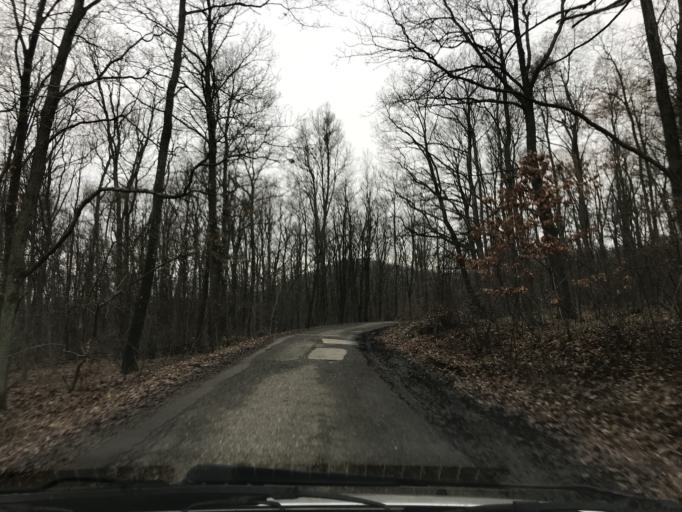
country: HU
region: Pest
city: Nagykovacsi
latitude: 47.6884
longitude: 18.9947
